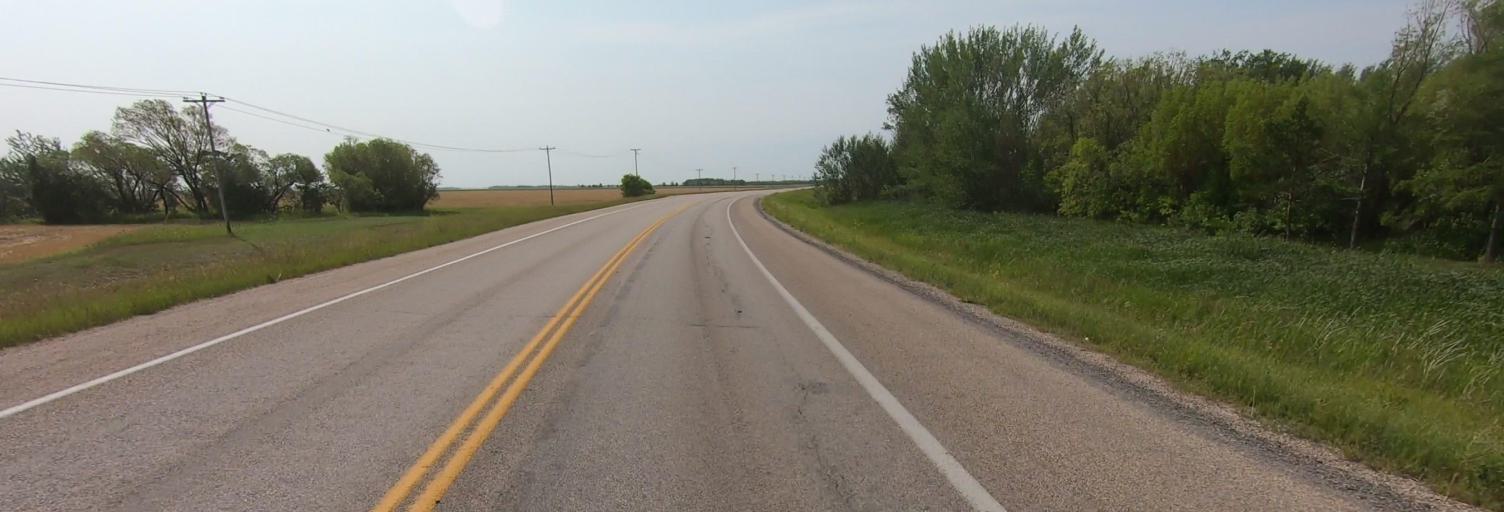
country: CA
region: Manitoba
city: Niverville
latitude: 49.6566
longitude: -97.1012
